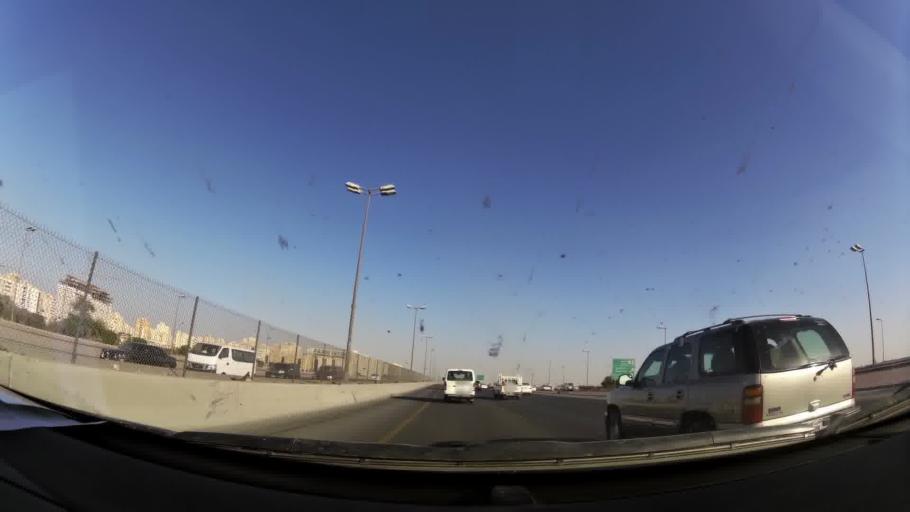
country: KW
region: Al Farwaniyah
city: Al Farwaniyah
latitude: 29.2661
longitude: 47.9495
